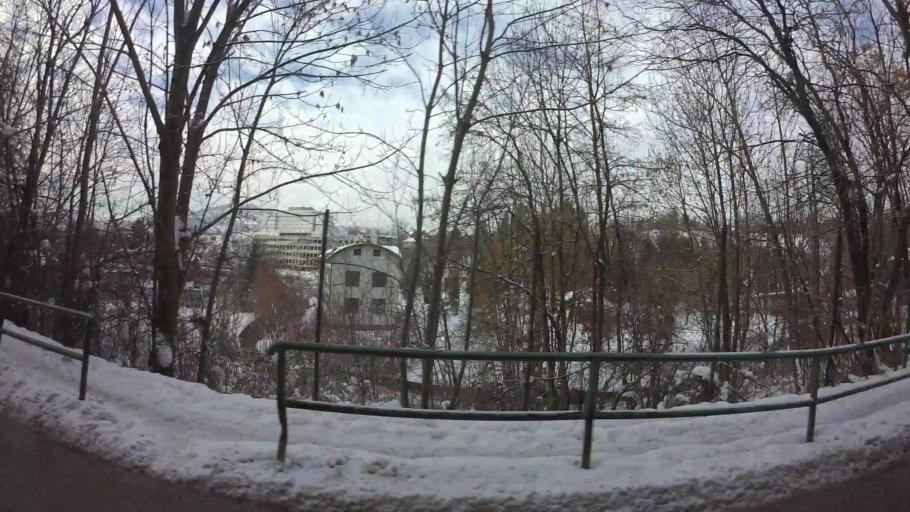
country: BA
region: Federation of Bosnia and Herzegovina
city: Kobilja Glava
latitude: 43.8776
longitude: 18.4134
